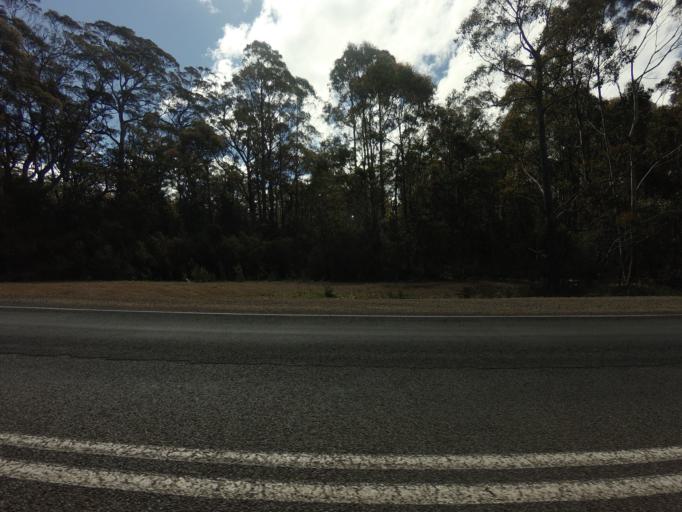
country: AU
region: Tasmania
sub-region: Northern Midlands
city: Evandale
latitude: -42.0092
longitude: 147.8879
